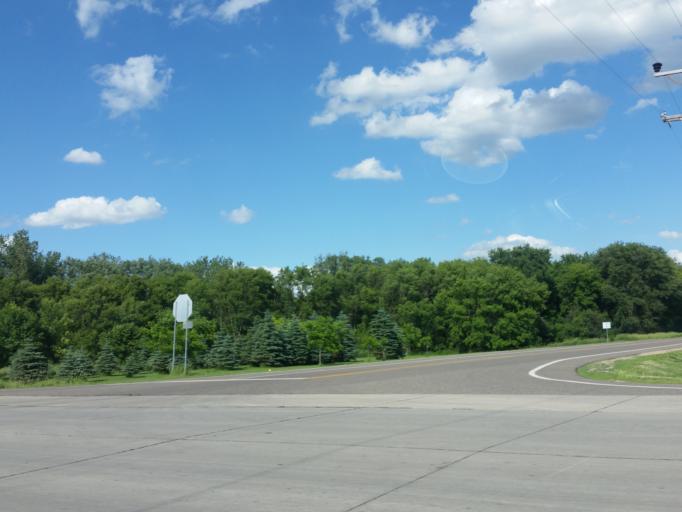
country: US
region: Minnesota
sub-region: Wright County
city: Cokato
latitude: 45.0654
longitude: -94.1904
